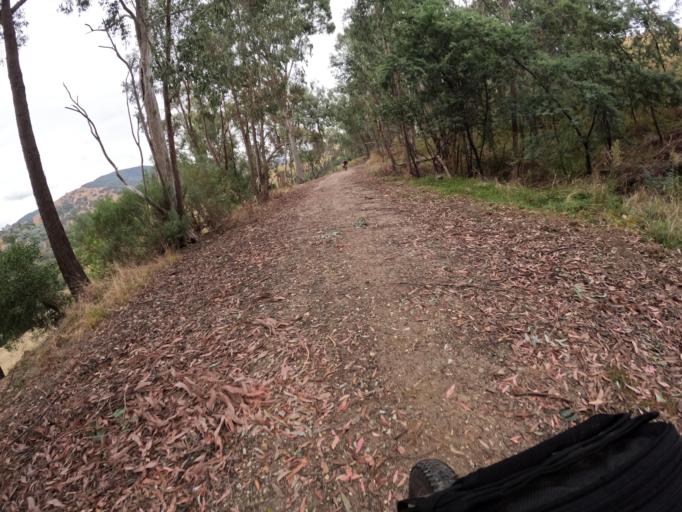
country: AU
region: New South Wales
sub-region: Albury Municipality
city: East Albury
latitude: -36.1796
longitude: 147.3796
